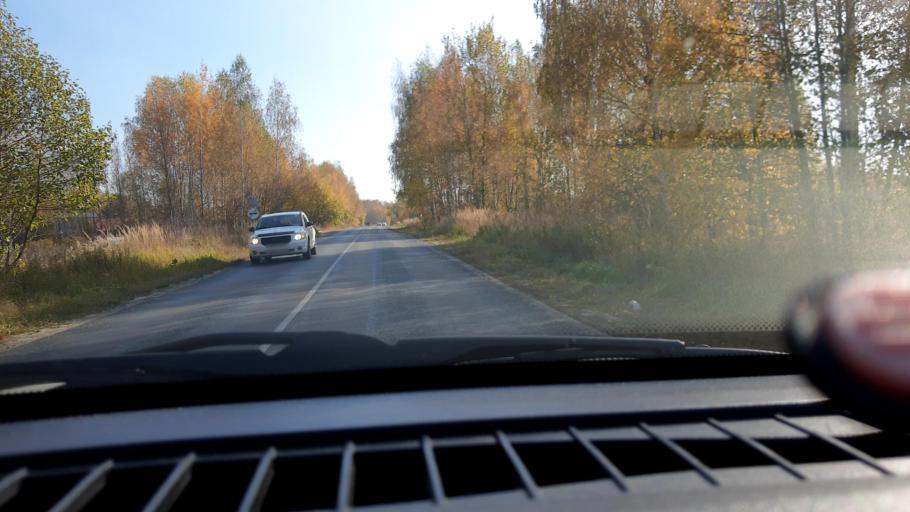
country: RU
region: Nizjnij Novgorod
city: Neklyudovo
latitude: 56.4389
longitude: 43.9135
